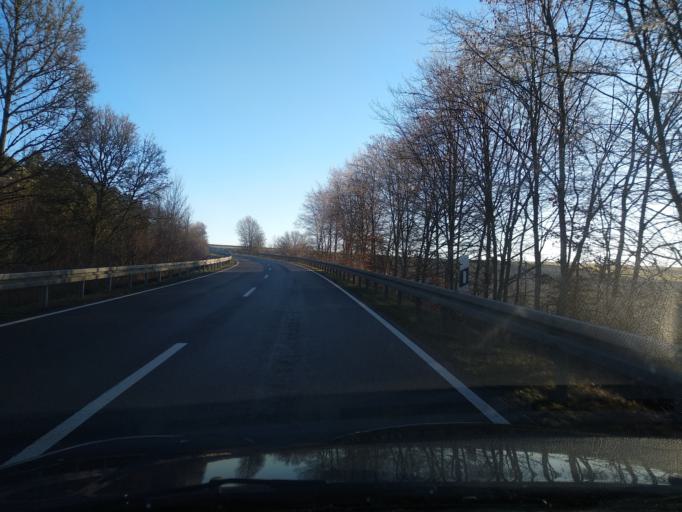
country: DE
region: Baden-Wuerttemberg
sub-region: Regierungsbezirk Stuttgart
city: Deckenpfronn
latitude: 48.6624
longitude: 8.8023
